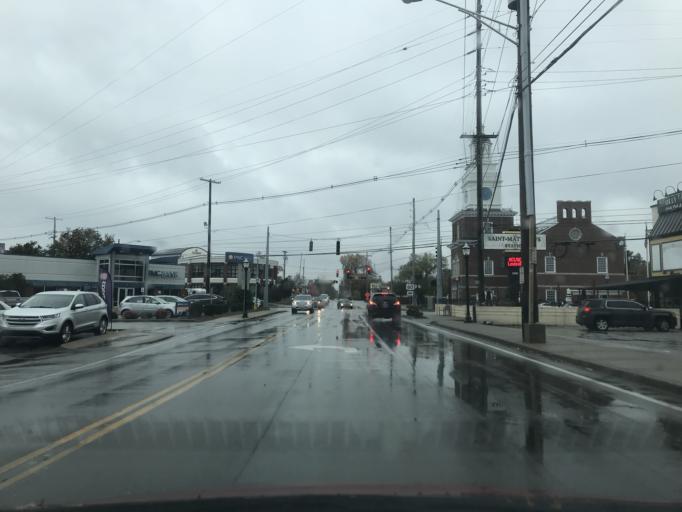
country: US
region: Kentucky
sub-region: Jefferson County
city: Saint Matthews
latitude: 38.2523
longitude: -85.6549
